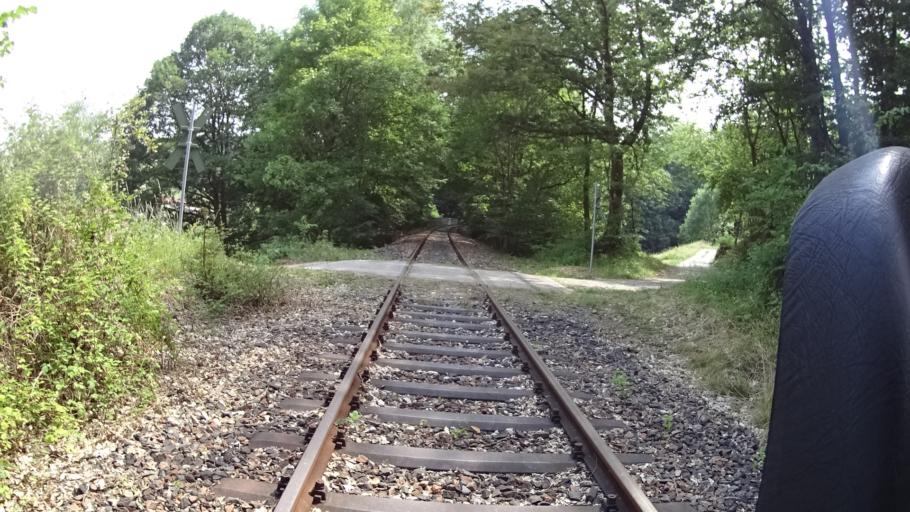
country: DE
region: Hesse
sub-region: Regierungsbezirk Darmstadt
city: Wald-Michelbach
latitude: 49.5666
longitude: 8.7972
